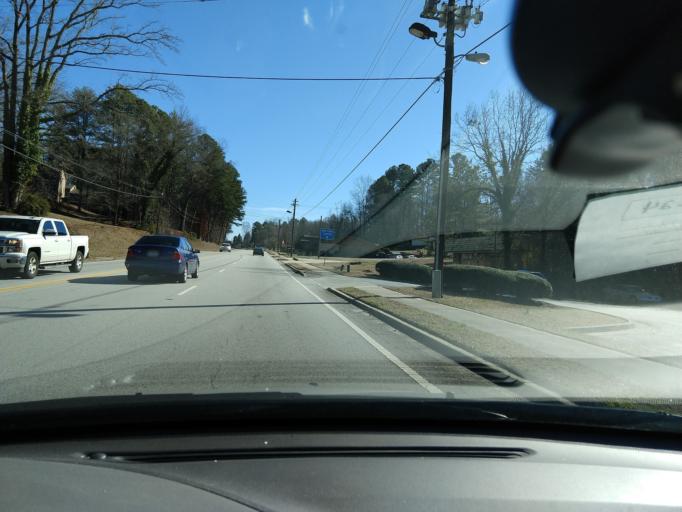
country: US
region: Georgia
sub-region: Stephens County
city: Toccoa
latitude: 34.5902
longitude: -83.3427
